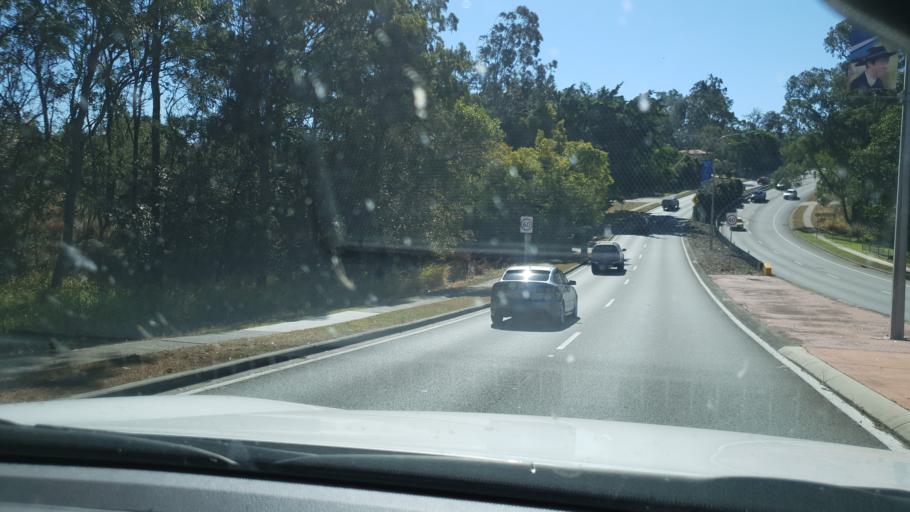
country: AU
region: Queensland
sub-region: Brisbane
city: Everton Park
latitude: -27.3936
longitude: 152.9853
